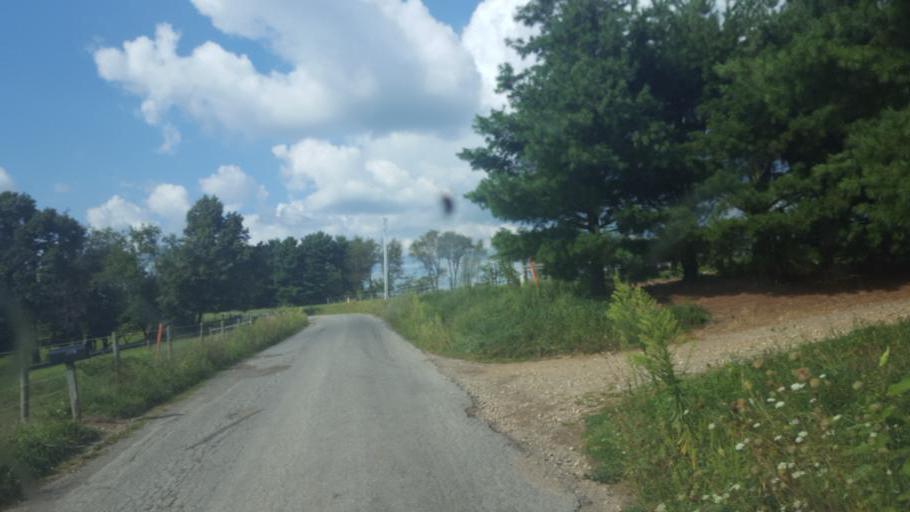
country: US
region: Ohio
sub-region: Knox County
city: Oak Hill
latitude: 40.4038
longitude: -82.2486
